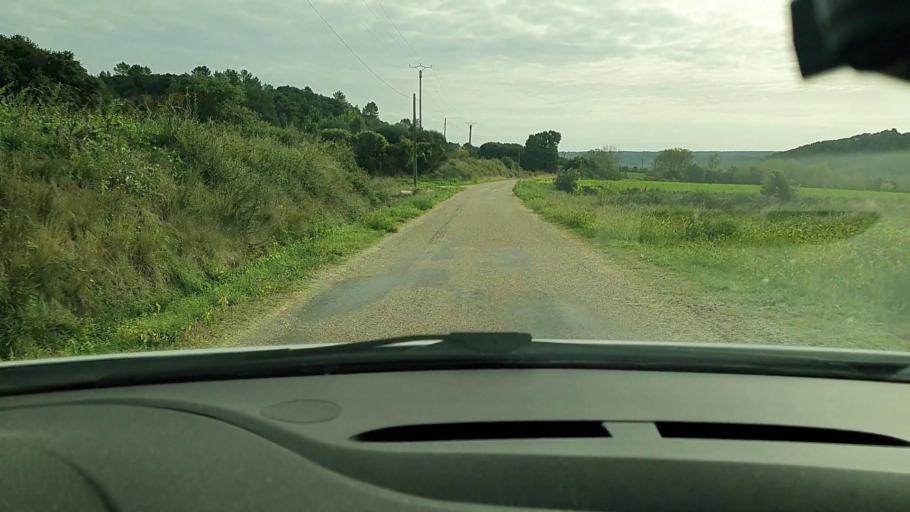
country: FR
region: Languedoc-Roussillon
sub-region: Departement du Gard
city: Montaren-et-Saint-Mediers
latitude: 44.0903
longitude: 4.3410
